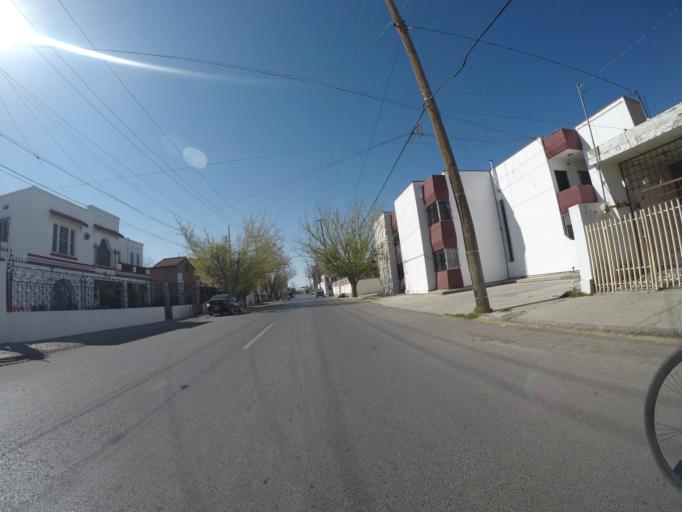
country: MX
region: Chihuahua
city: Ciudad Juarez
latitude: 31.7403
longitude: -106.4738
